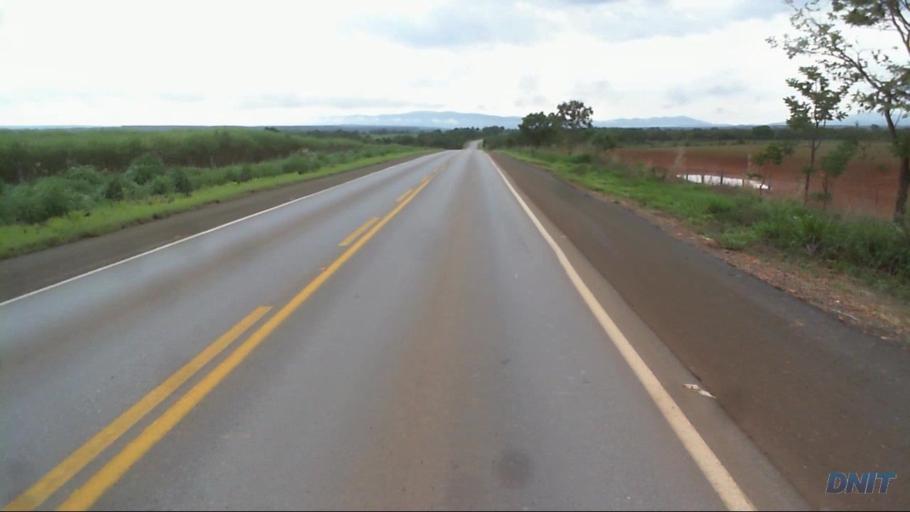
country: BR
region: Goias
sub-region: Uruacu
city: Uruacu
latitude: -14.7221
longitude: -49.0991
